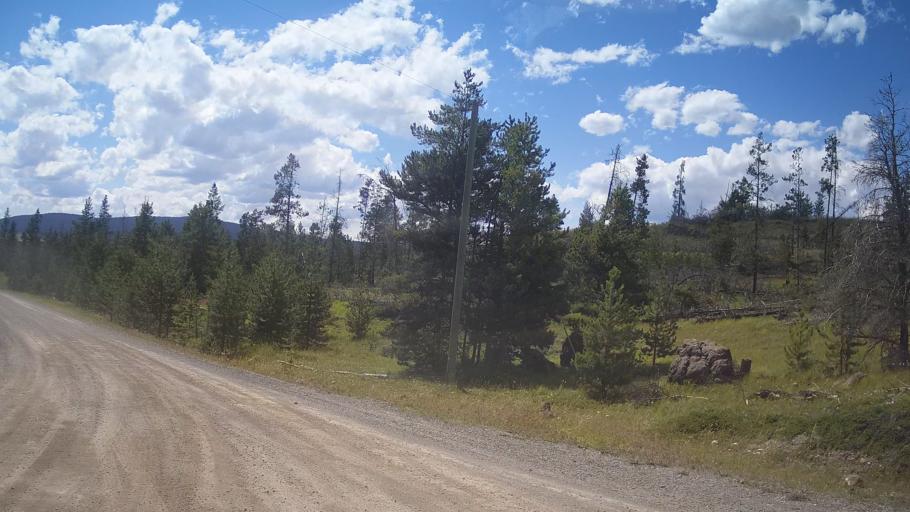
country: CA
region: British Columbia
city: Lillooet
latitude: 51.3358
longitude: -121.9711
